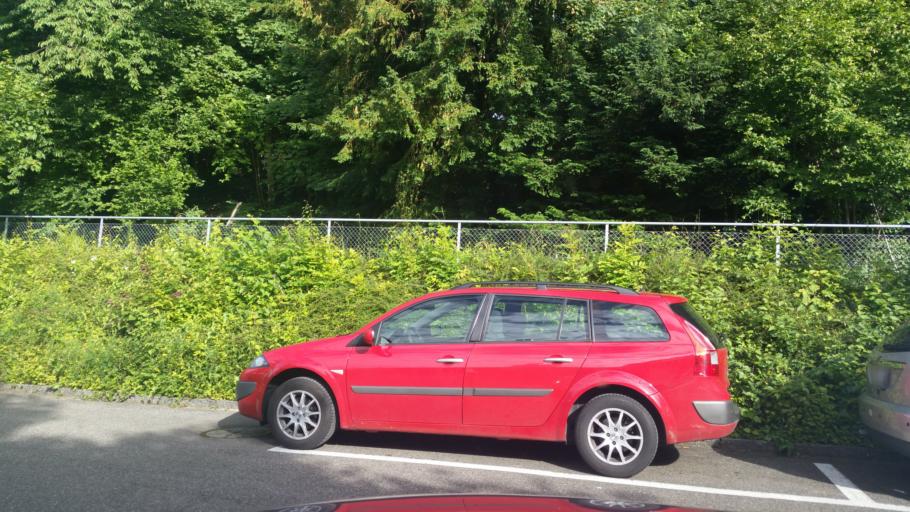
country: CH
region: Thurgau
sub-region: Frauenfeld District
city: Frauenfeld
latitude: 47.5526
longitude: 8.8965
